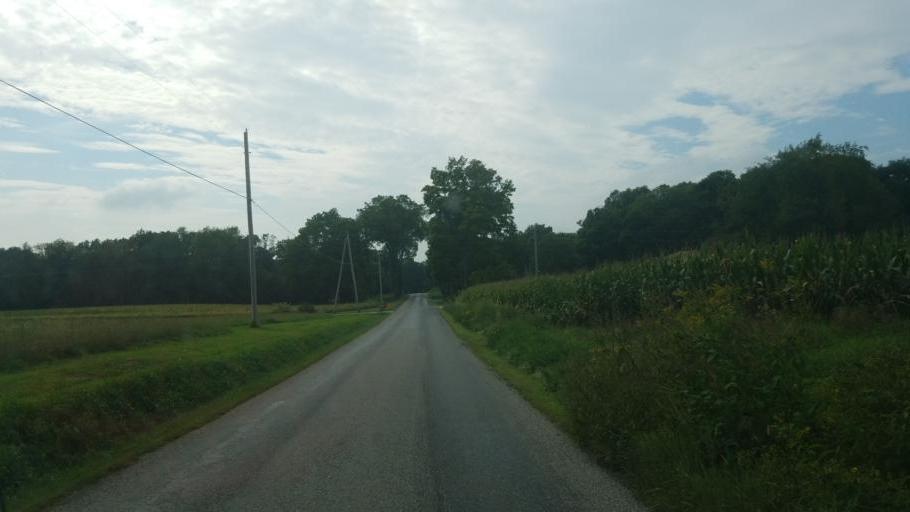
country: US
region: Ohio
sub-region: Wayne County
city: Wooster
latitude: 40.9011
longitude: -81.9970
